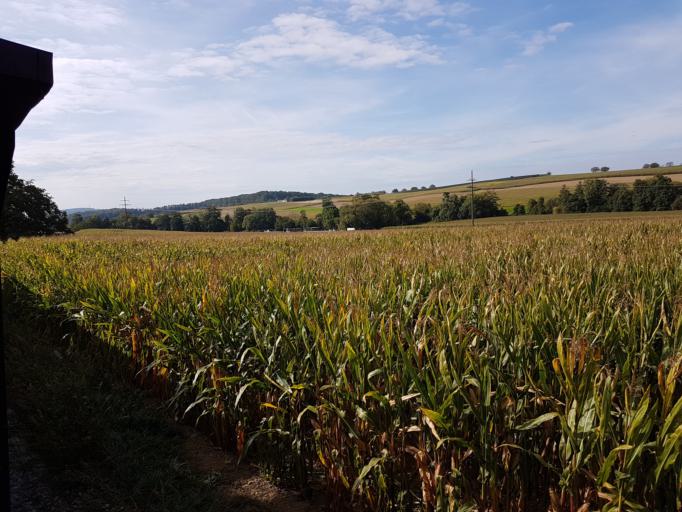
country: DE
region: Baden-Wuerttemberg
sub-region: Freiburg Region
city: Wittlingen
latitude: 47.6813
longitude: 7.6450
